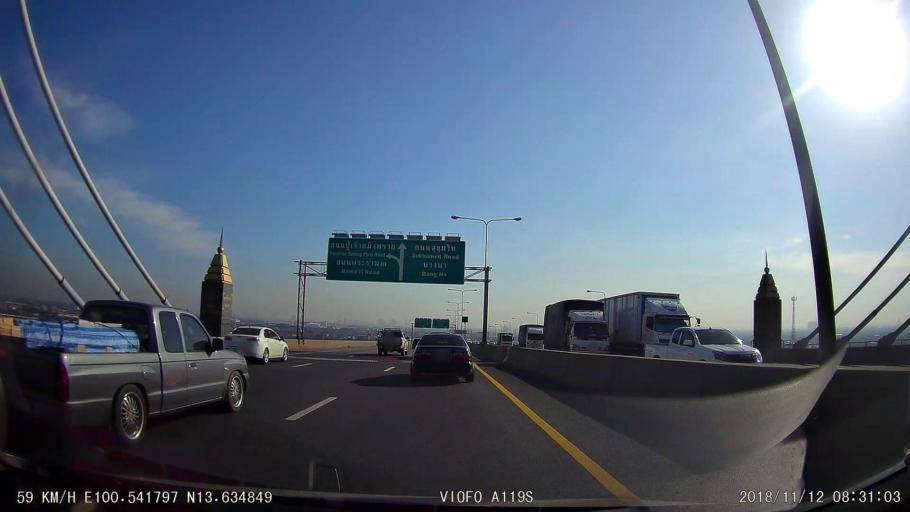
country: TH
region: Samut Prakan
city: Phra Pradaeng
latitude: 13.6352
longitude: 100.5425
